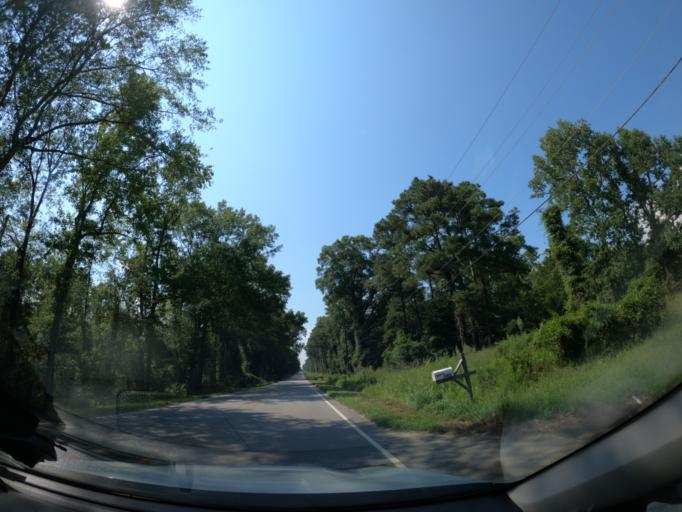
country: US
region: South Carolina
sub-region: Richland County
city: Hopkins
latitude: 33.9094
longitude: -80.9370
